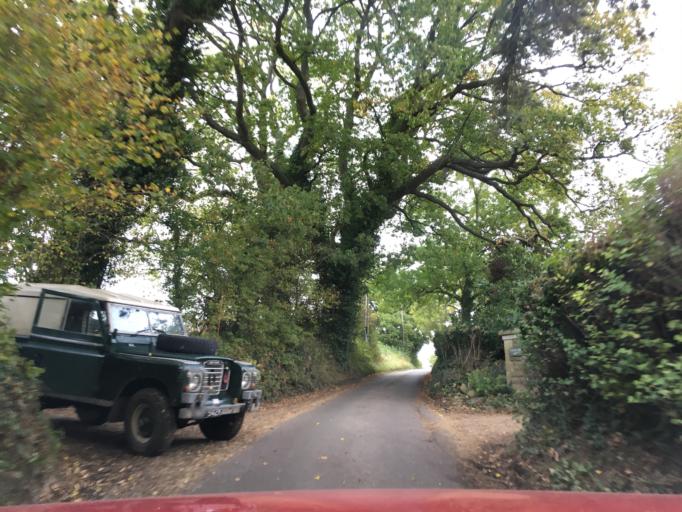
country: GB
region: England
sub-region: South Gloucestershire
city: Wickwar
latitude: 51.5979
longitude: -2.3912
